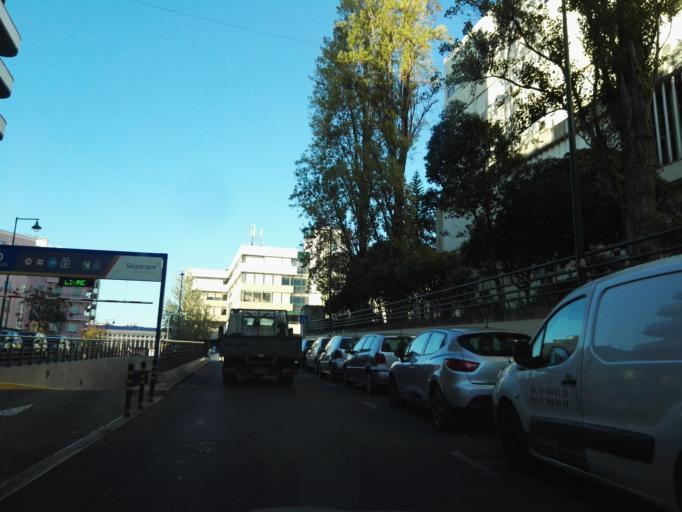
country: PT
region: Lisbon
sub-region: Lisbon
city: Lisbon
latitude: 38.7360
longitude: -9.1404
